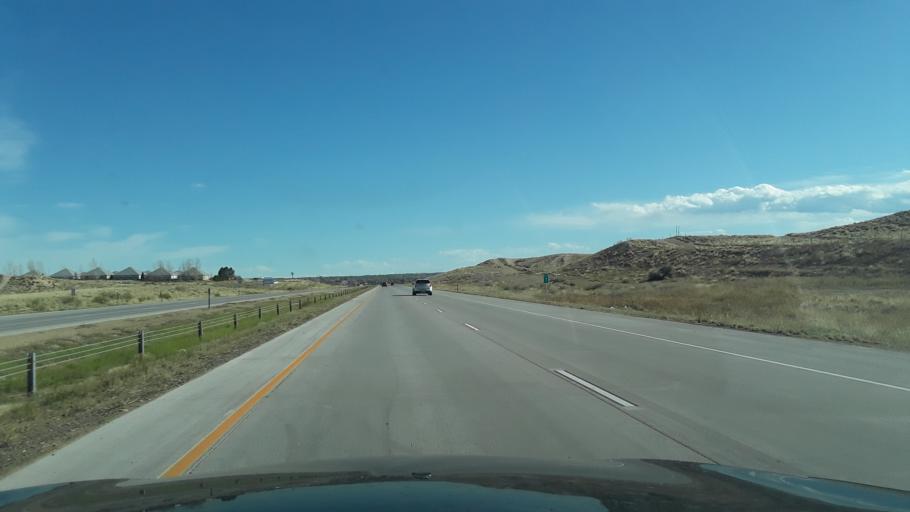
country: US
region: Colorado
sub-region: Pueblo County
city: Pueblo
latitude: 38.2907
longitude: -104.6637
